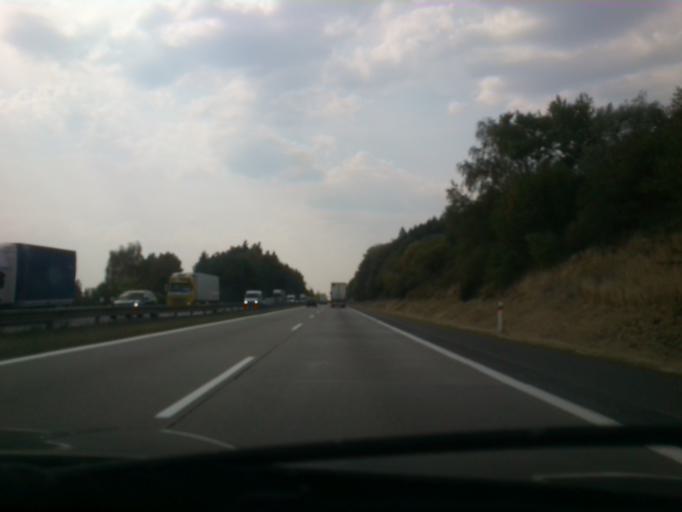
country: CZ
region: Central Bohemia
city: Divisov
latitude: 49.8349
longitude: 14.8475
